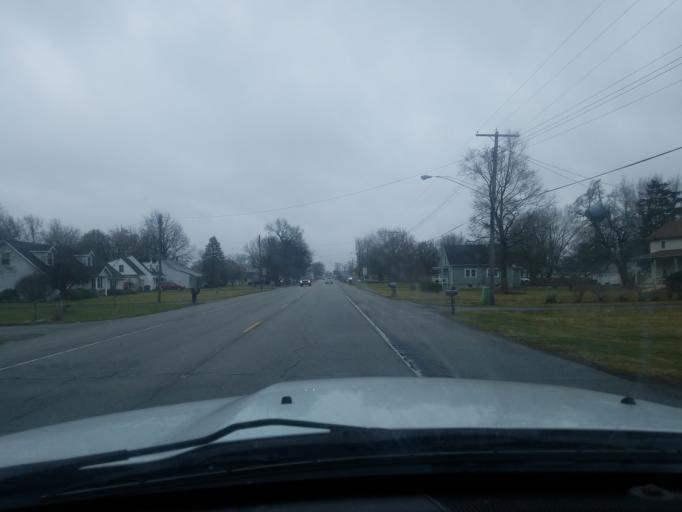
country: US
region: Indiana
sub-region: Wells County
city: Ossian
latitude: 40.8870
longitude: -85.1665
